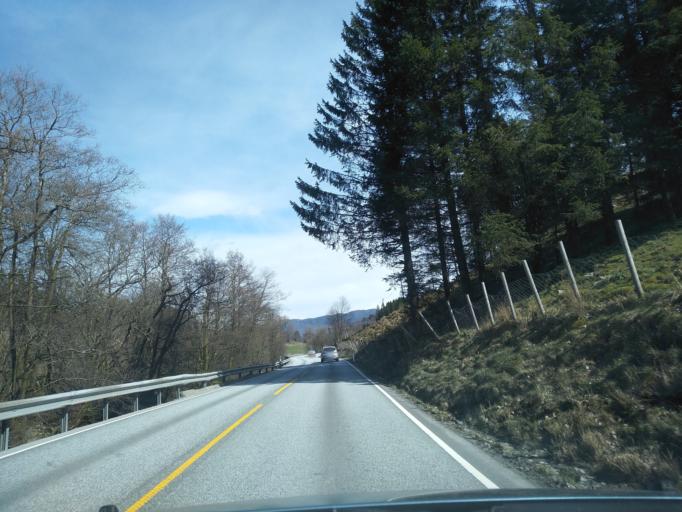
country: NO
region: Rogaland
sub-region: Vindafjord
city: Olen
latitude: 59.5863
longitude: 5.7213
